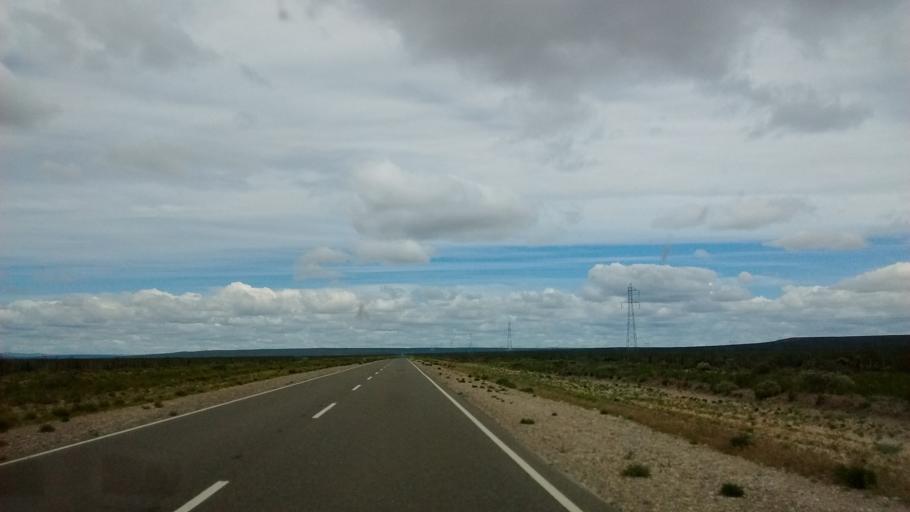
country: AR
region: Neuquen
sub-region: Departamento de Picun Leufu
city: Picun Leufu
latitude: -39.6758
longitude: -69.4523
